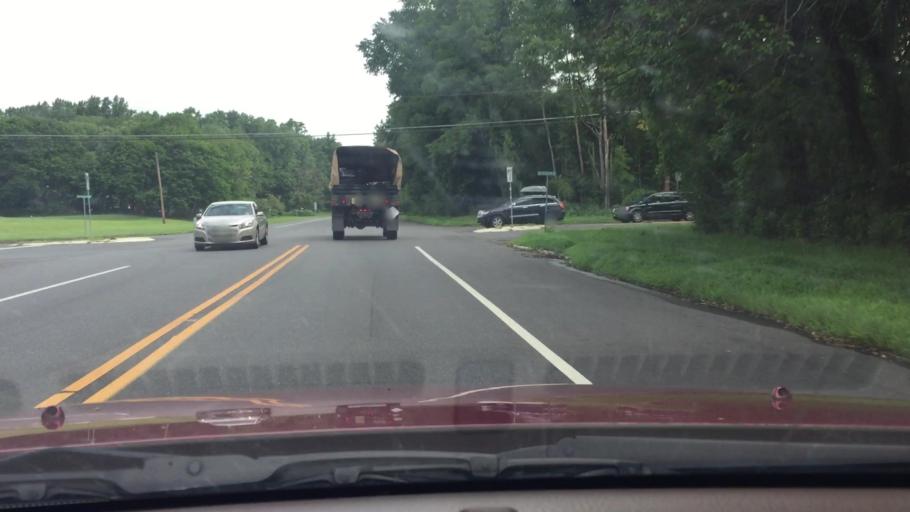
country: US
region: New Jersey
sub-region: Burlington County
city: Fort Dix
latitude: 40.0644
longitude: -74.6530
